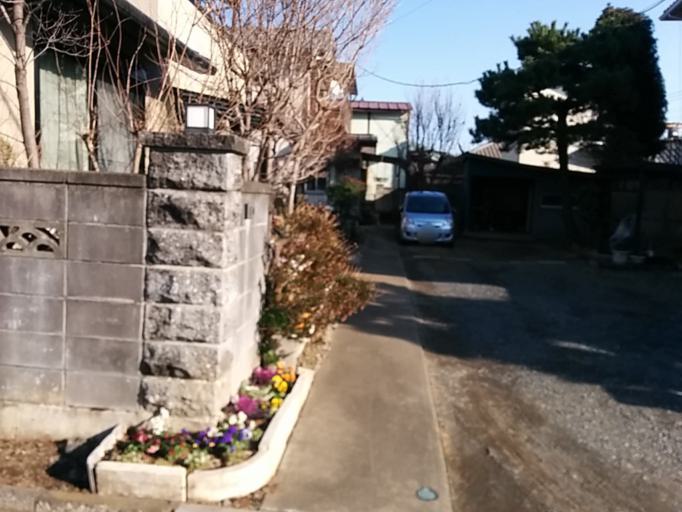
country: JP
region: Saitama
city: Kawagoe
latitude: 35.9214
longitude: 139.4773
